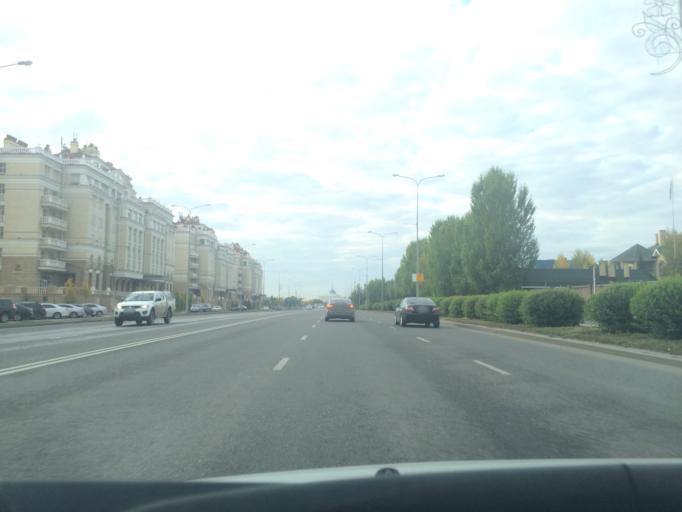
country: KZ
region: Astana Qalasy
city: Astana
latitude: 51.1451
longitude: 71.4449
